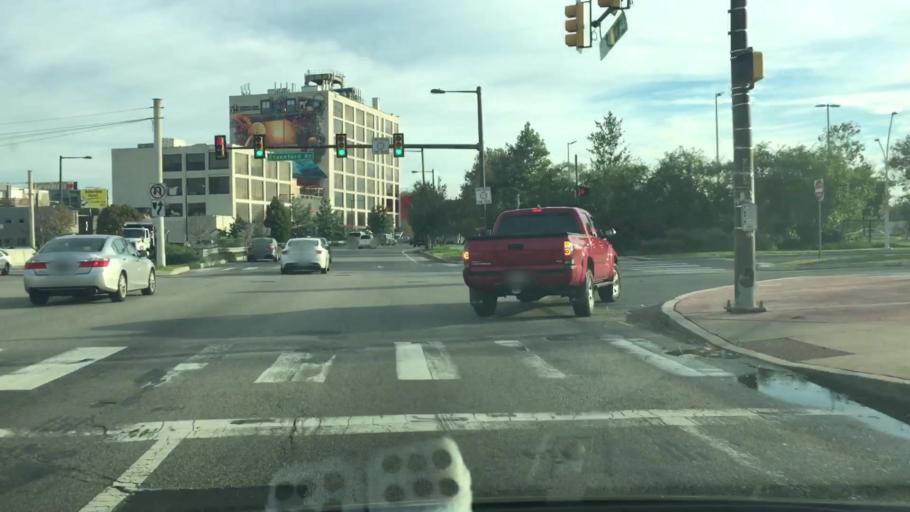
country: US
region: Pennsylvania
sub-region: Philadelphia County
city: Philadelphia
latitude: 39.9643
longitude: -75.1344
